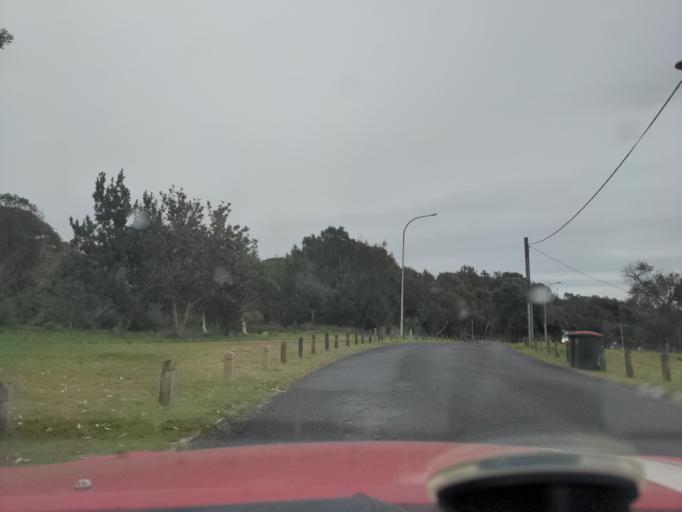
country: AU
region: New South Wales
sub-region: Randwick
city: Malabar
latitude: -33.9509
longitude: 151.2542
